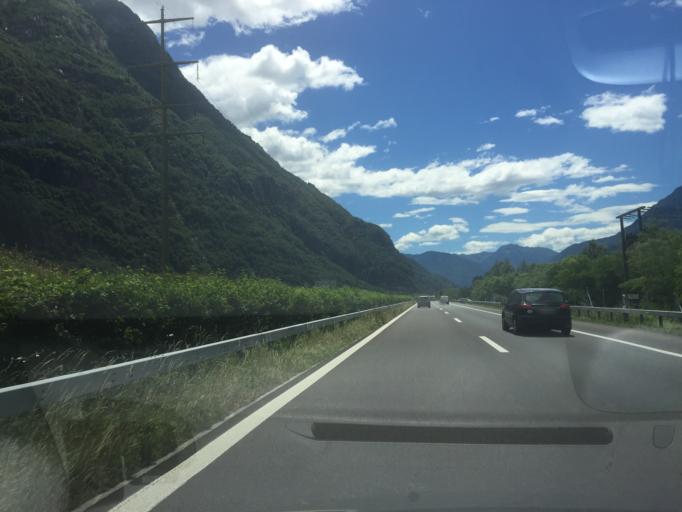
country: CH
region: Ticino
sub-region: Riviera District
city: Biasca
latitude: 46.3406
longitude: 8.9699
